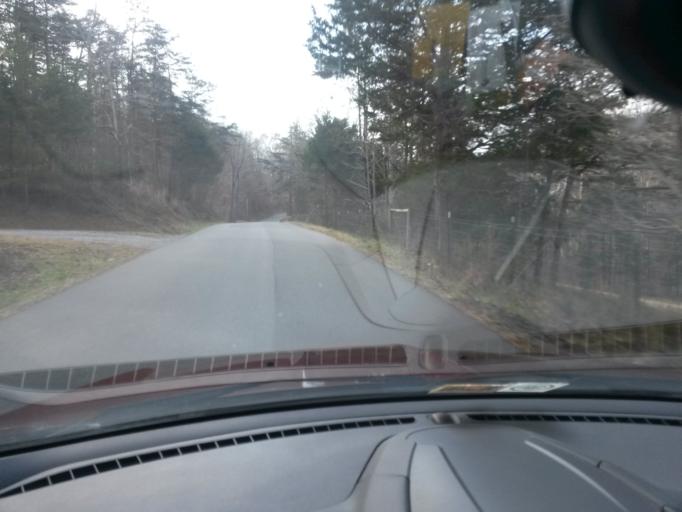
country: US
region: Virginia
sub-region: Botetourt County
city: Fincastle
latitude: 37.5891
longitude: -79.8666
